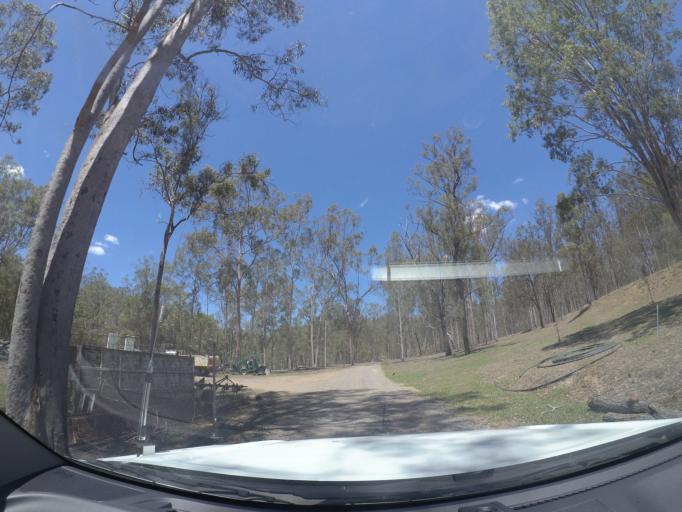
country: AU
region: Queensland
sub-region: Ipswich
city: Deebing Heights
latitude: -27.7650
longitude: 152.8102
